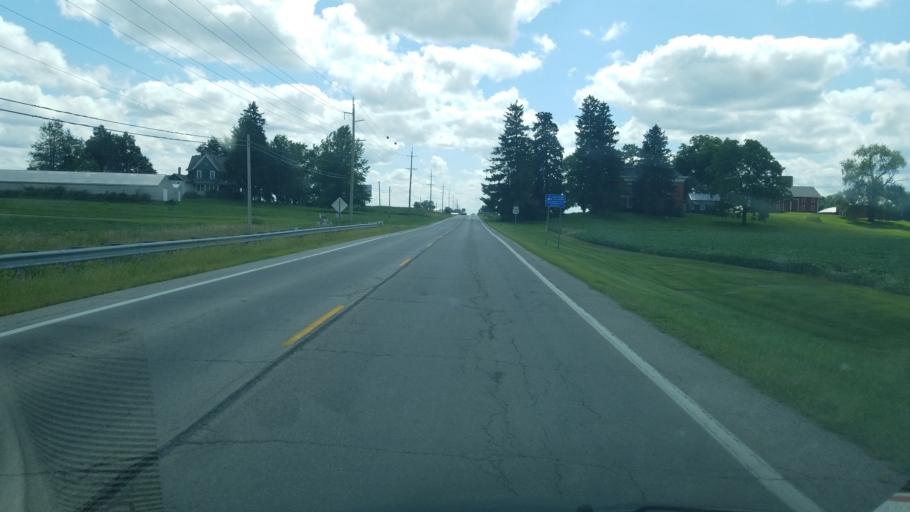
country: US
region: Ohio
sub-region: Henry County
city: Napoleon
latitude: 41.3777
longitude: -84.1207
